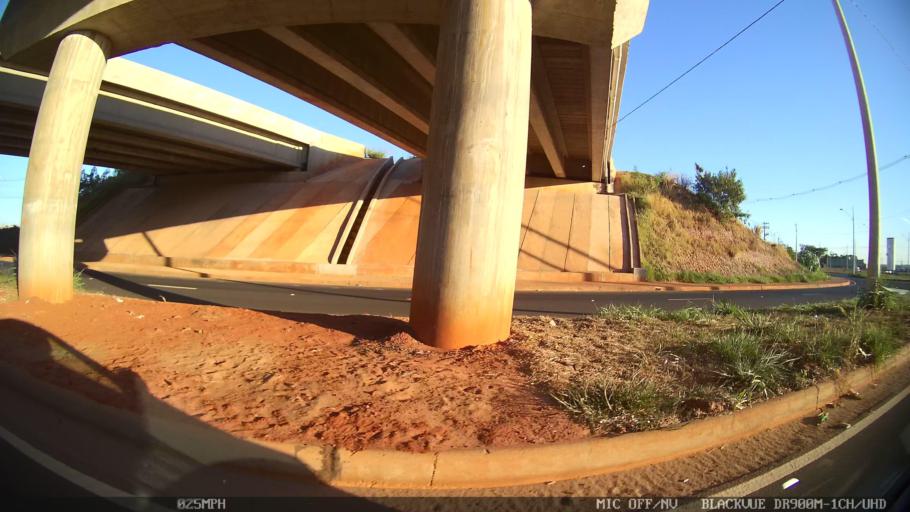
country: BR
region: Sao Paulo
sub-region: Sao Jose Do Rio Preto
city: Sao Jose do Rio Preto
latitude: -20.7611
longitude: -49.3467
